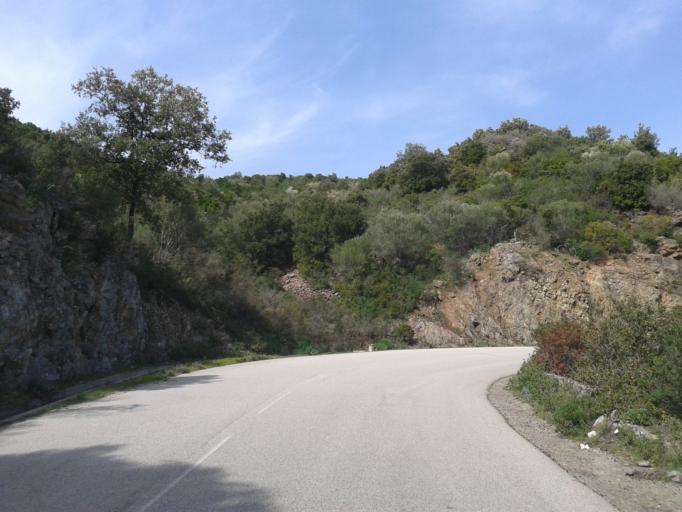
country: FR
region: Corsica
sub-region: Departement de la Haute-Corse
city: Monticello
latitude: 42.6560
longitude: 9.1153
